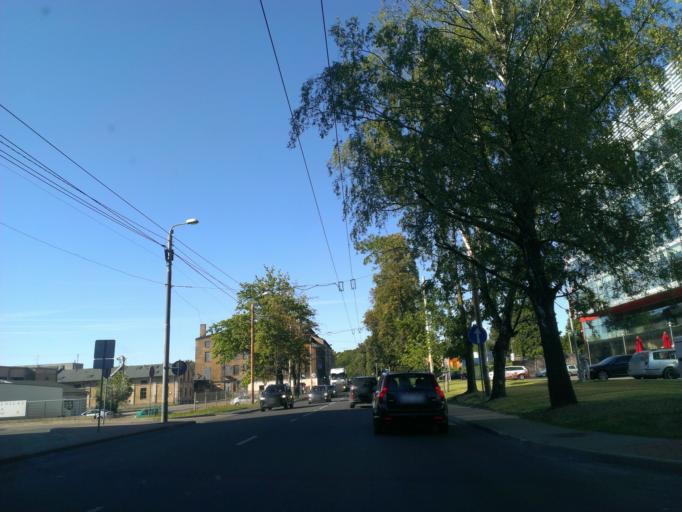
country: LV
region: Riga
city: Riga
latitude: 56.9774
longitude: 24.1359
